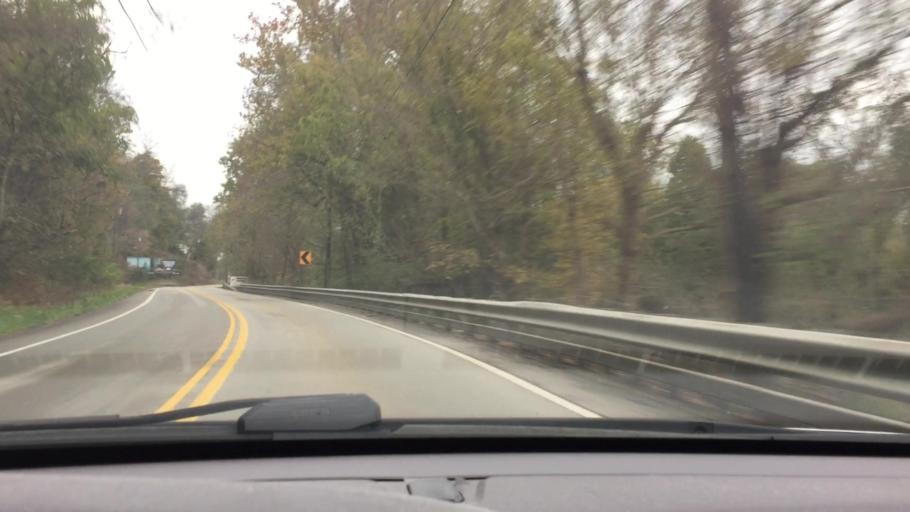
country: US
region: Pennsylvania
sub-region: Fayette County
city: Fairhope
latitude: 40.1062
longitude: -79.8479
